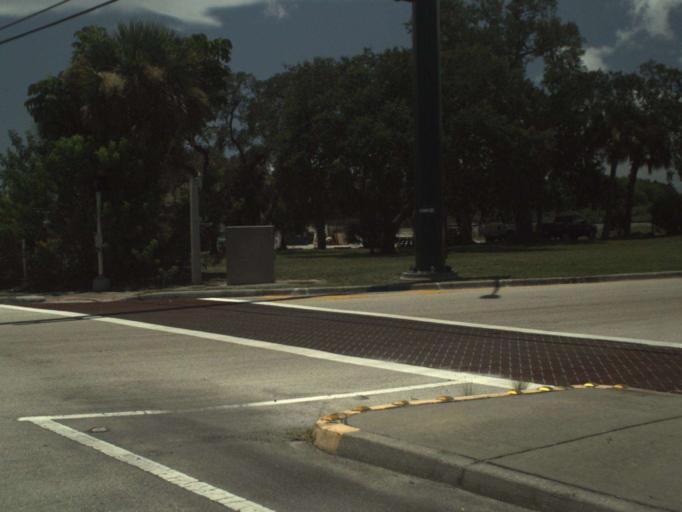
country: US
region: Florida
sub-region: Indian River County
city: Sebastian
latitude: 27.8122
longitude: -80.4677
